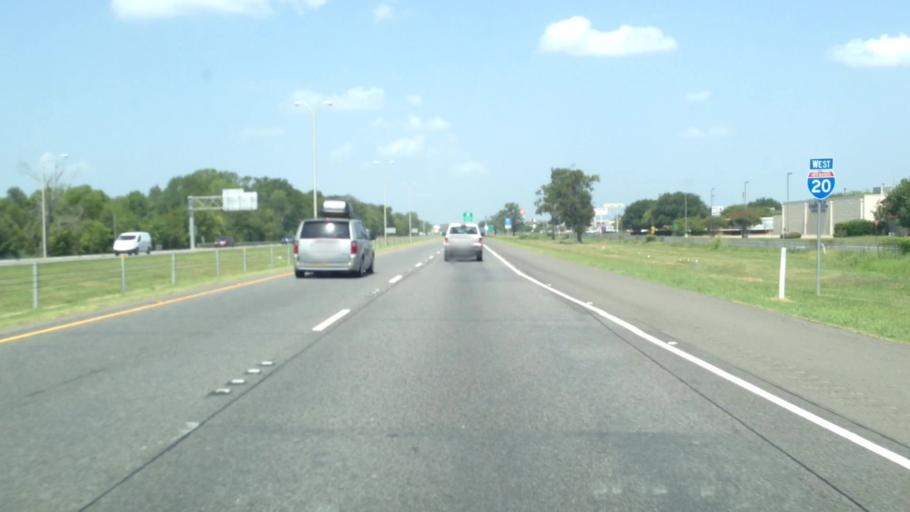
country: US
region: Louisiana
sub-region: Ouachita Parish
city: Lakeshore
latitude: 32.4955
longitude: -92.0610
